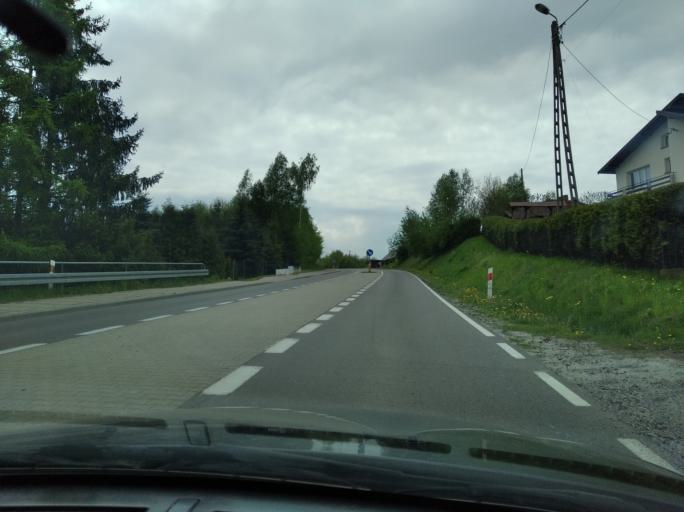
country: PL
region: Lesser Poland Voivodeship
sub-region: Powiat tarnowski
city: Tarnowiec
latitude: 49.9539
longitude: 21.0067
